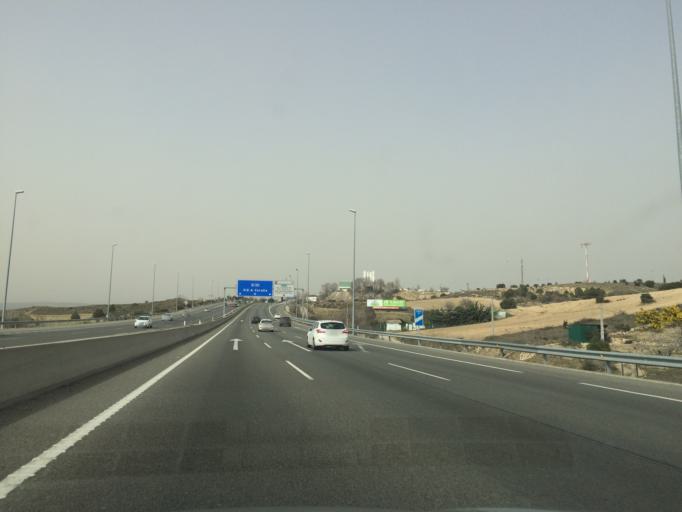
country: ES
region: Madrid
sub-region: Provincia de Madrid
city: Majadahonda
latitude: 40.4724
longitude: -3.8936
